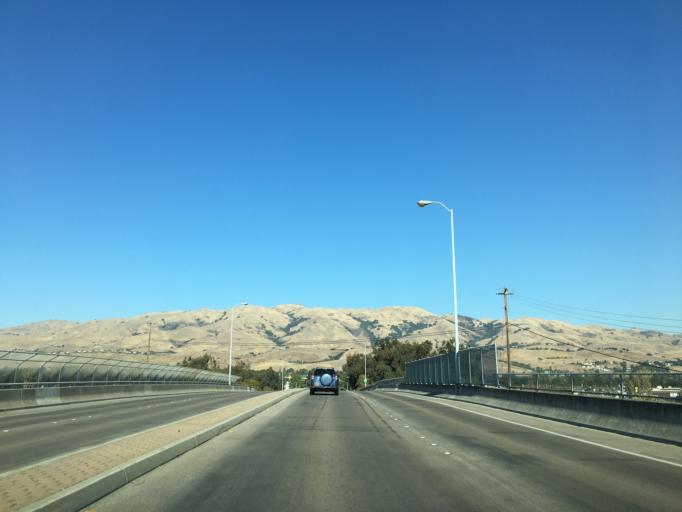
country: US
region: California
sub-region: Santa Clara County
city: Milpitas
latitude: 37.4423
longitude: -121.9094
